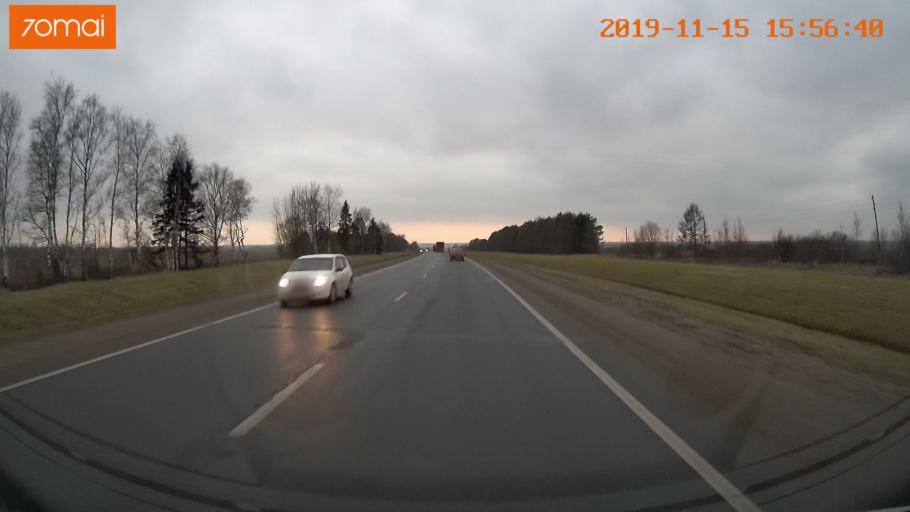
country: RU
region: Jaroslavl
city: Yaroslavl
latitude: 57.8395
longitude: 39.9711
